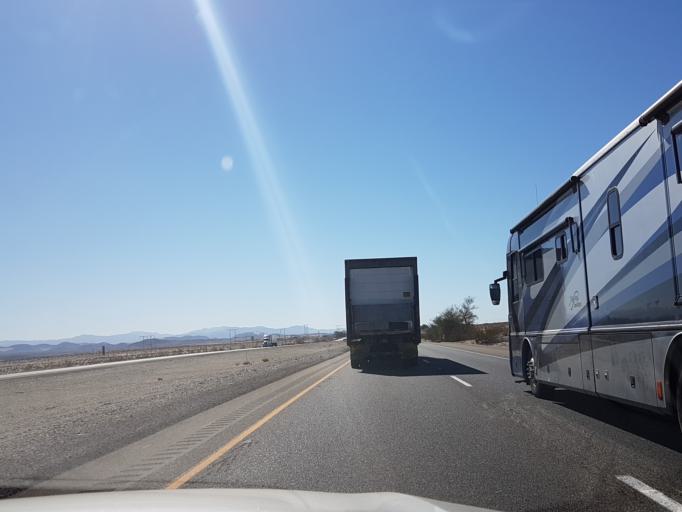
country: US
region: California
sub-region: San Bernardino County
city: Fort Irwin
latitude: 35.0410
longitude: -116.4585
